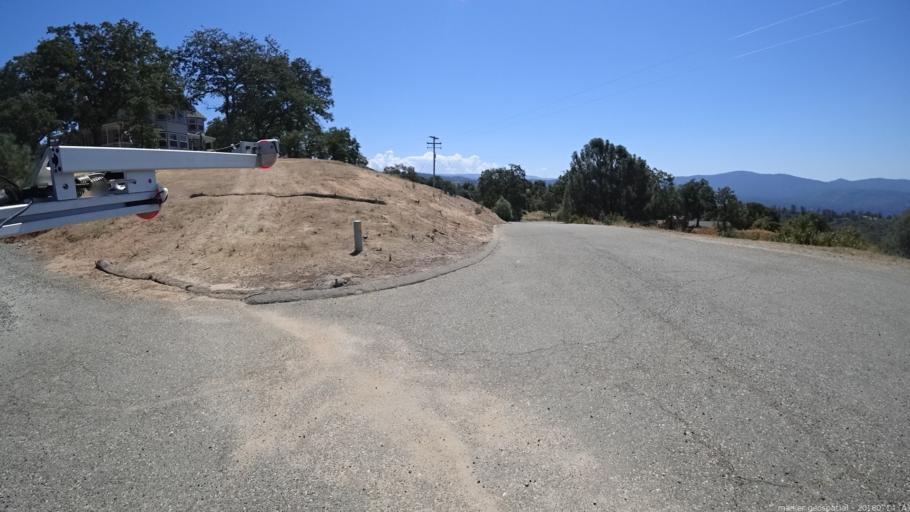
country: US
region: California
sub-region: Madera County
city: Oakhurst
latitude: 37.3617
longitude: -119.6600
